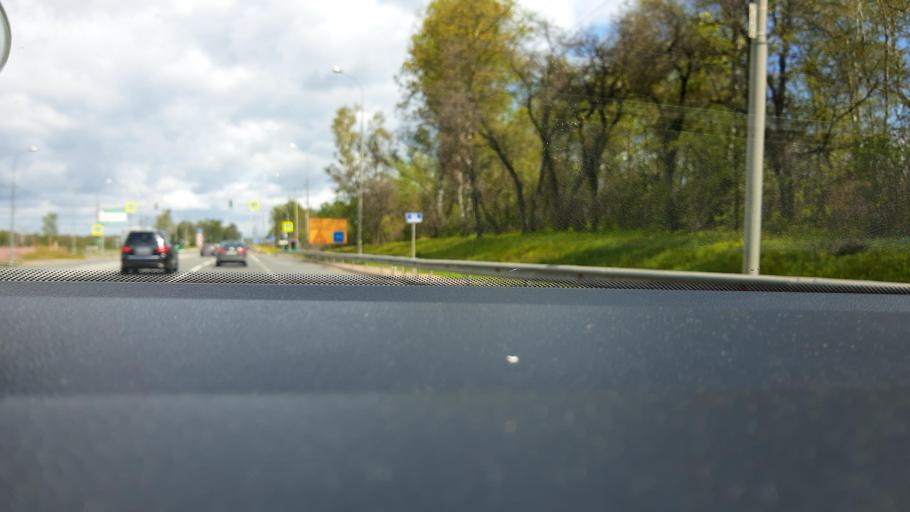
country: RU
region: Moskovskaya
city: Podosinki
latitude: 56.2077
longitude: 37.5229
